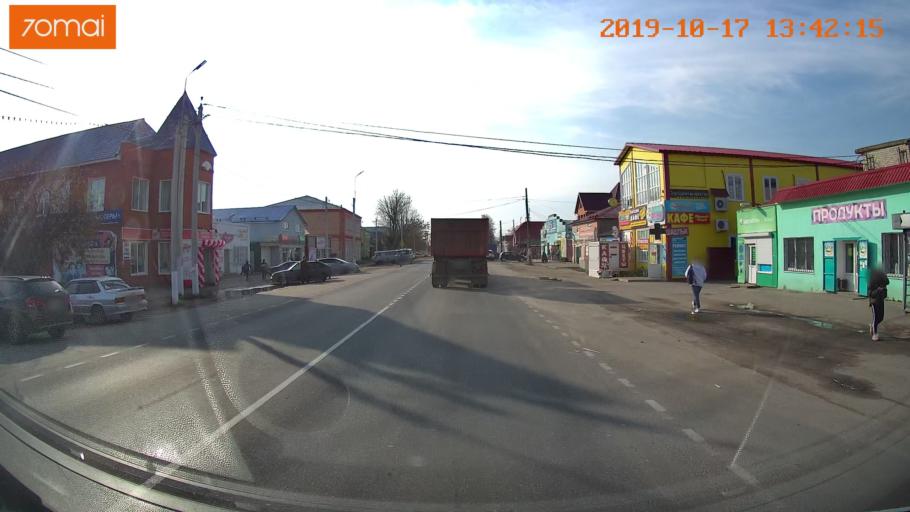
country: RU
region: Rjazan
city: Tuma
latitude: 55.1474
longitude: 40.5552
